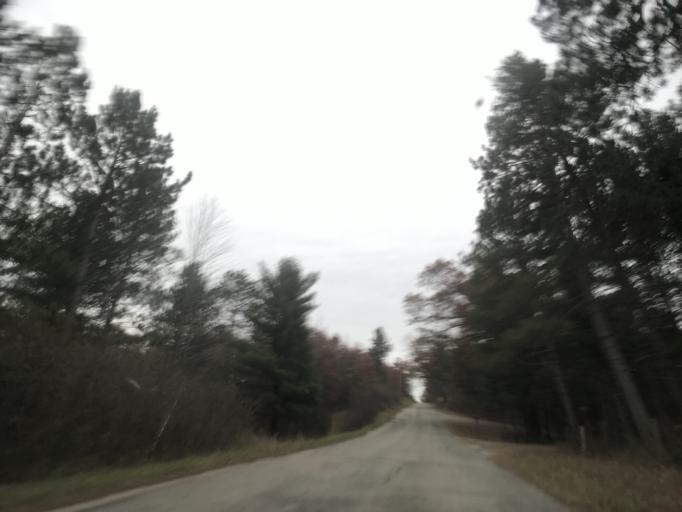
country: US
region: Wisconsin
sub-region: Oconto County
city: Gillett
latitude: 45.3239
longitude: -88.2763
